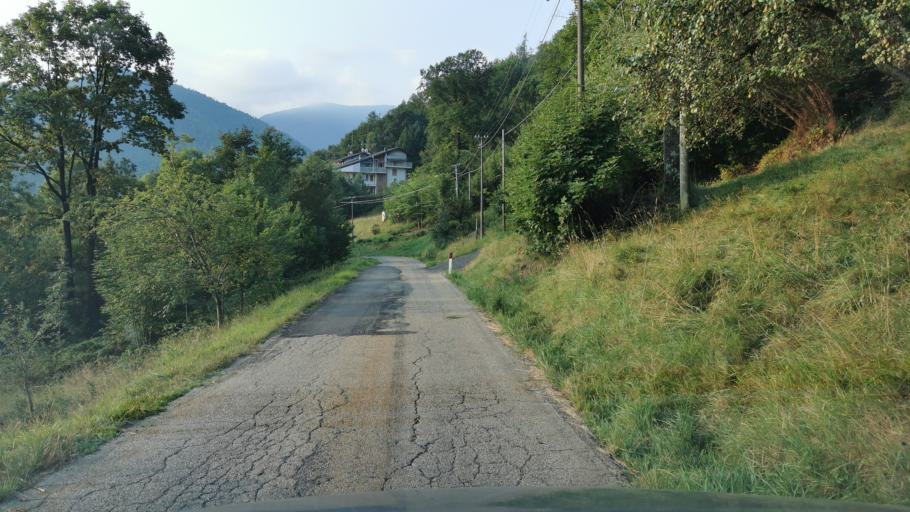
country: IT
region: Piedmont
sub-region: Provincia di Torino
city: La Villa
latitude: 45.2619
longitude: 7.4307
